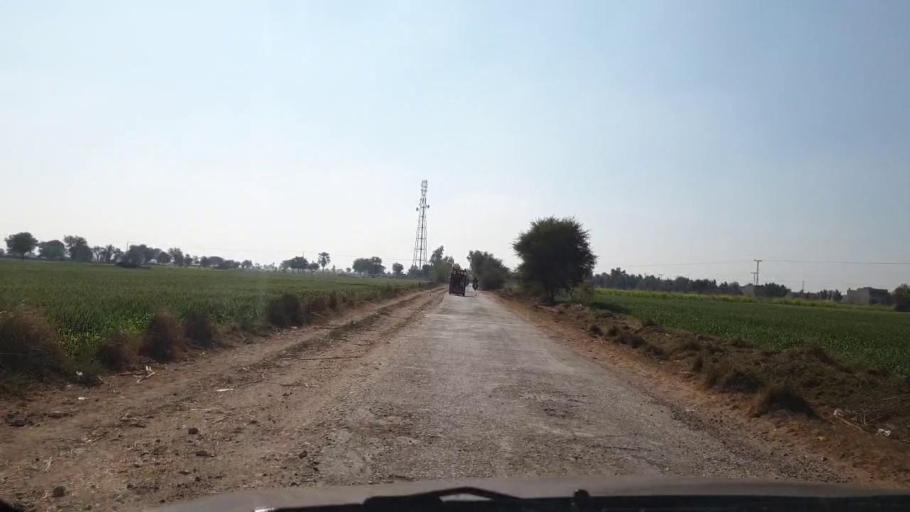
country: PK
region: Sindh
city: Sinjhoro
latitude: 25.9406
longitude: 68.7470
